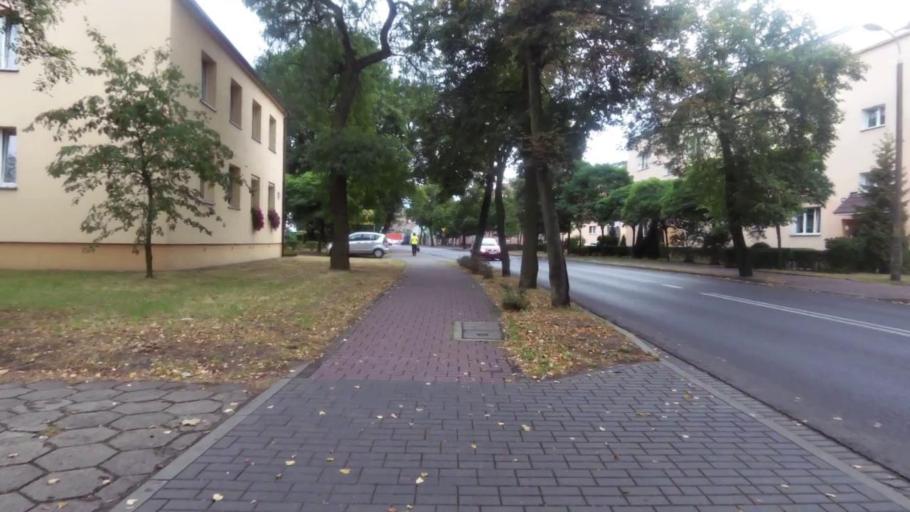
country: PL
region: Lubusz
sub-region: Powiat gorzowski
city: Kostrzyn nad Odra
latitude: 52.5934
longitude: 14.6421
